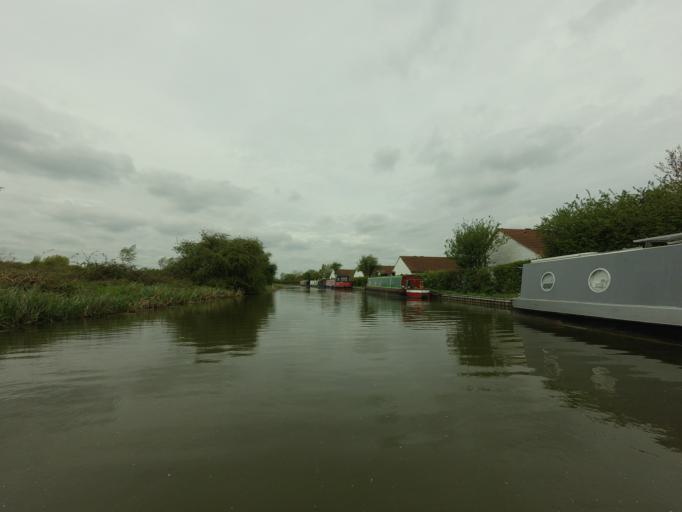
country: GB
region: England
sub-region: Milton Keynes
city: Newport Pagnell
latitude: 52.0713
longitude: -0.7456
